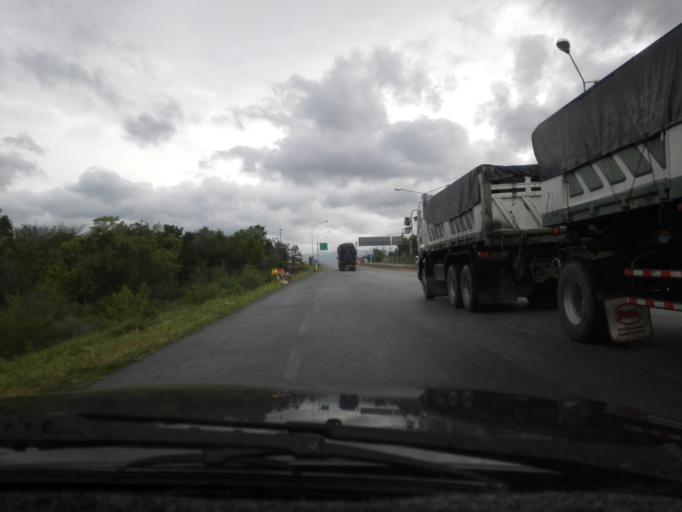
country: TH
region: Tak
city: Tak
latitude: 16.8412
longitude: 99.1133
